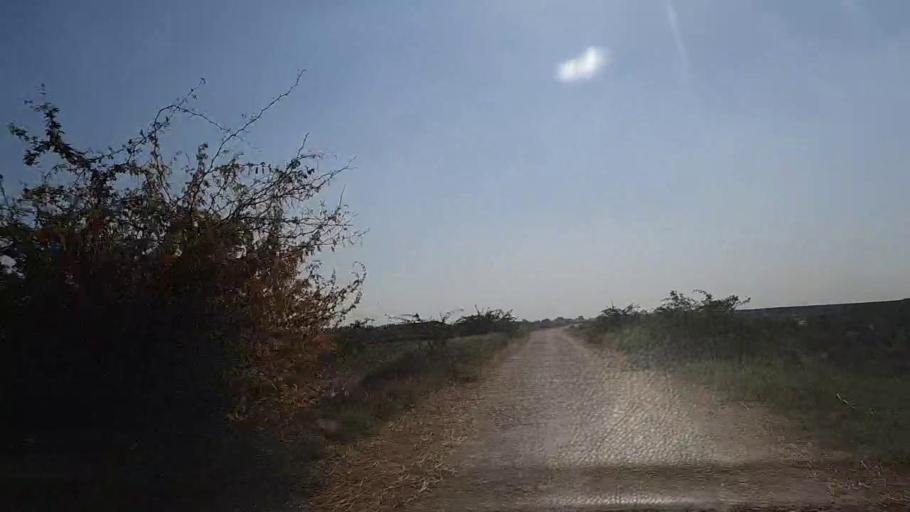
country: PK
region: Sindh
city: Daro Mehar
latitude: 24.7631
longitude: 68.0658
